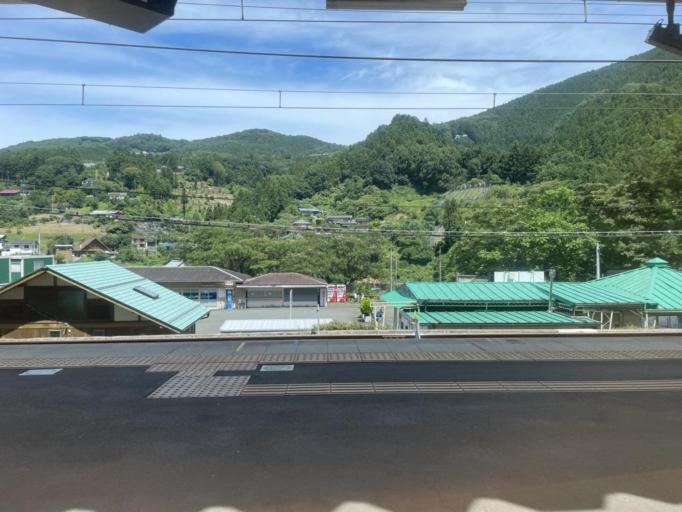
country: JP
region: Saitama
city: Chichibu
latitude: 35.9765
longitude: 139.1370
